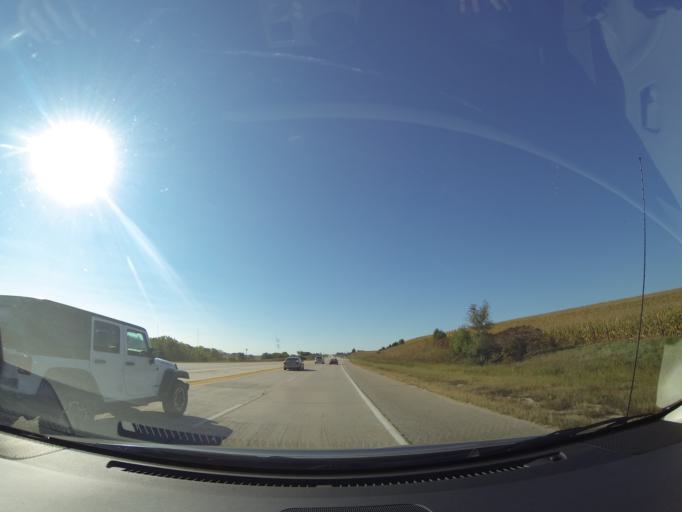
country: US
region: Nebraska
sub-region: Sarpy County
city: Gretna
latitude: 41.1165
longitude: -96.2532
